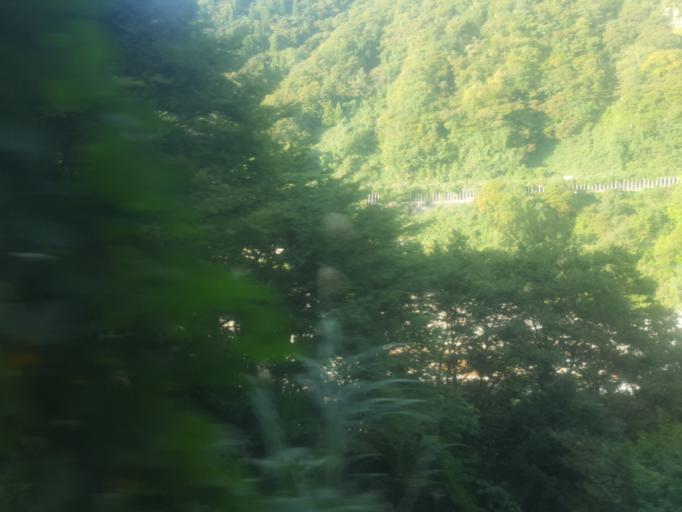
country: JP
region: Toyama
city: Kamiichi
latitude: 36.5836
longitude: 137.4374
